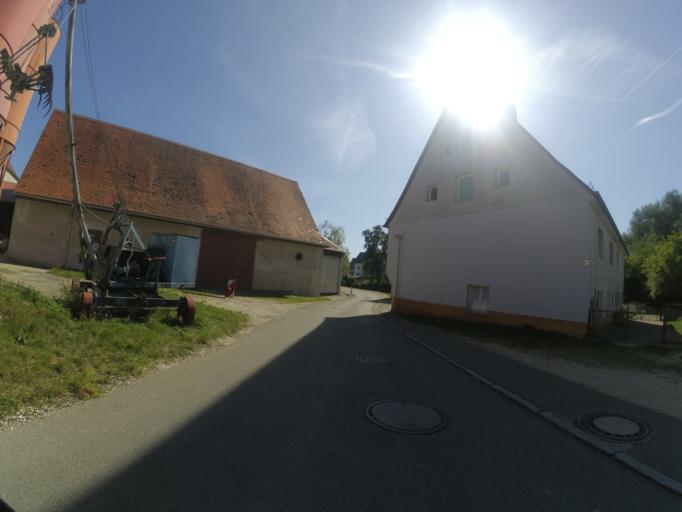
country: DE
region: Baden-Wuerttemberg
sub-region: Tuebingen Region
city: Langenau
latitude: 48.4974
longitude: 10.1121
